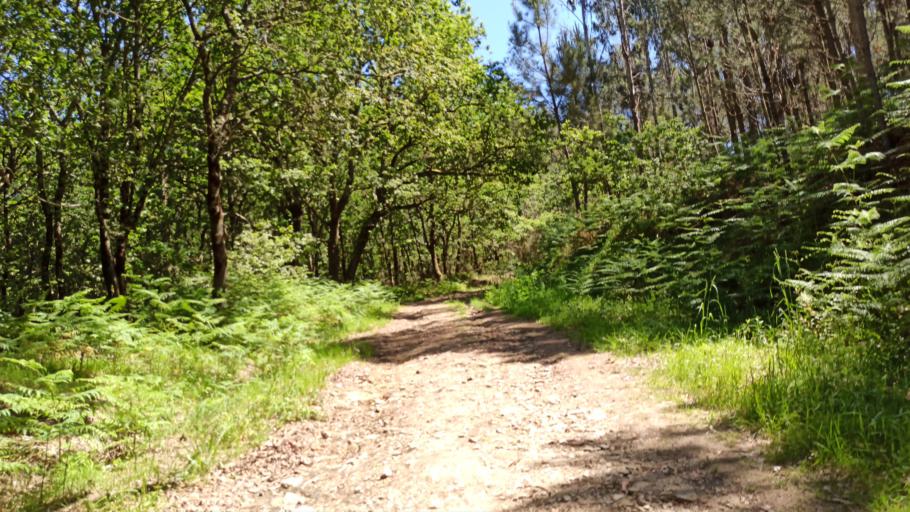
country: ES
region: Galicia
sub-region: Provincia da Coruna
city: Negreira
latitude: 42.9187
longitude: -8.7247
